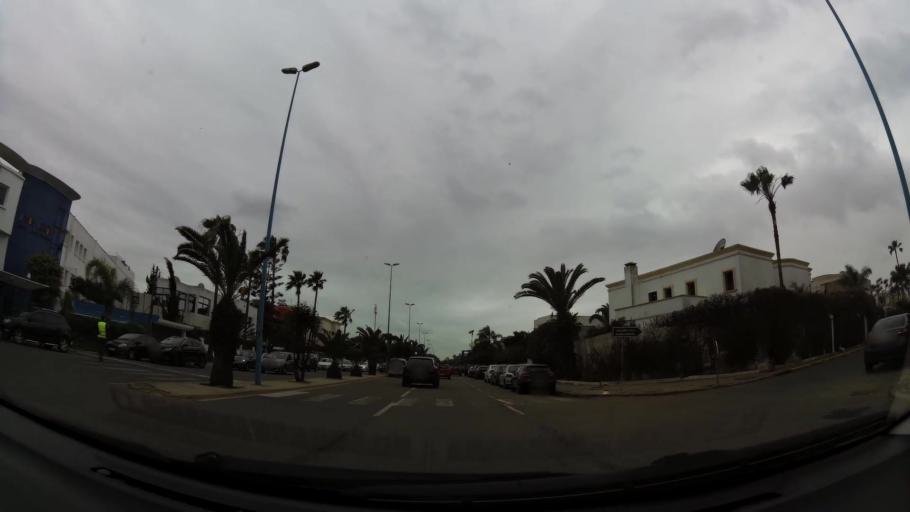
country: MA
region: Grand Casablanca
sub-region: Casablanca
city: Casablanca
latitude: 33.5965
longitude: -7.6549
